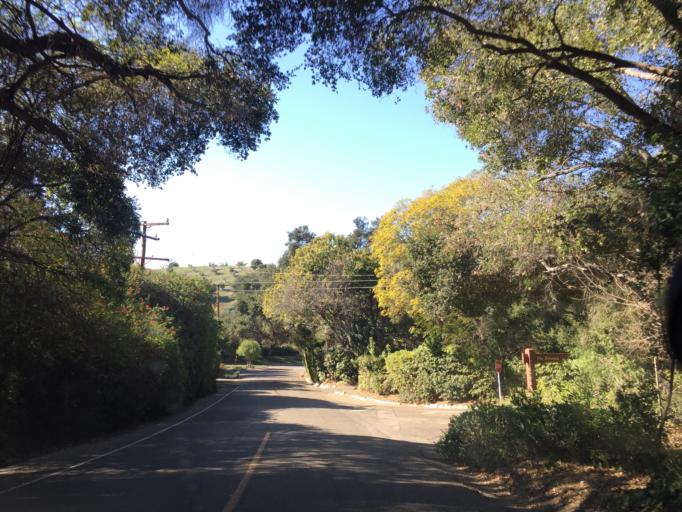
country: US
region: California
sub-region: Santa Barbara County
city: Mission Canyon
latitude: 34.4331
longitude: -119.7674
